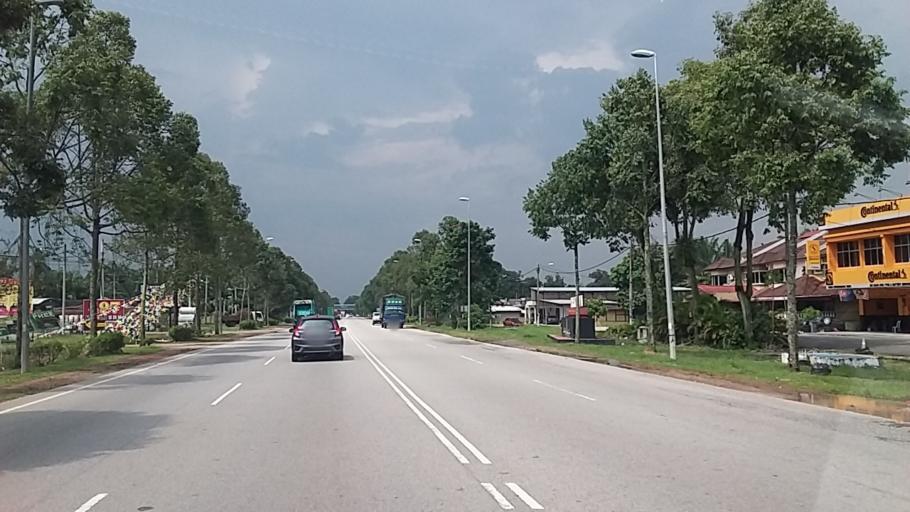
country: MY
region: Johor
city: Parit Raja
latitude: 1.8689
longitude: 103.1230
